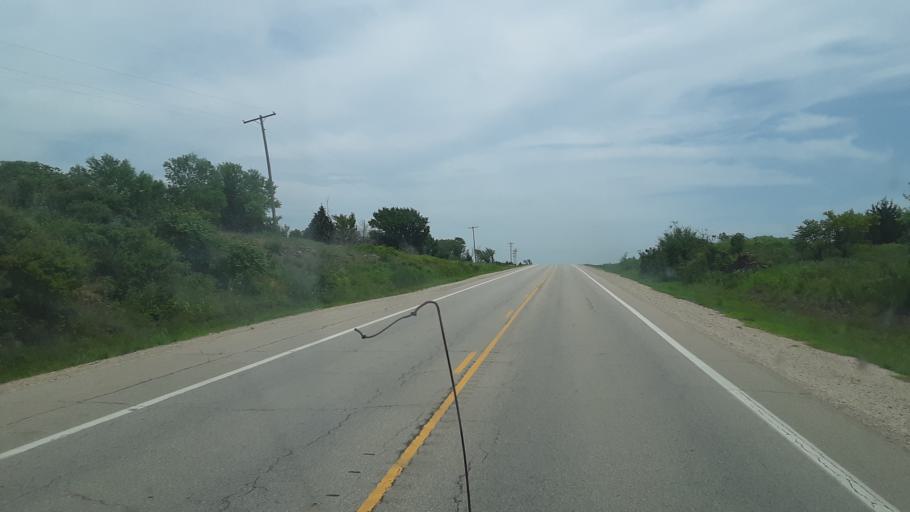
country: US
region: Kansas
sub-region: Woodson County
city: Yates Center
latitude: 37.8363
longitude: -95.9260
